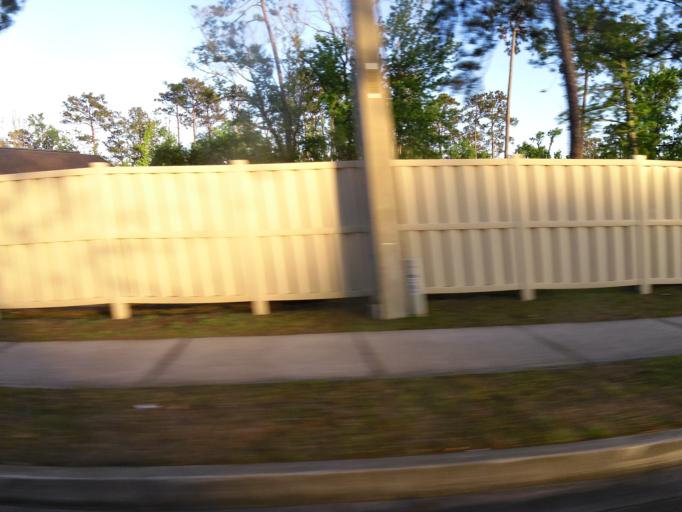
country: US
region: Florida
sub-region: Duval County
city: Jacksonville
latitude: 30.2604
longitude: -81.5783
